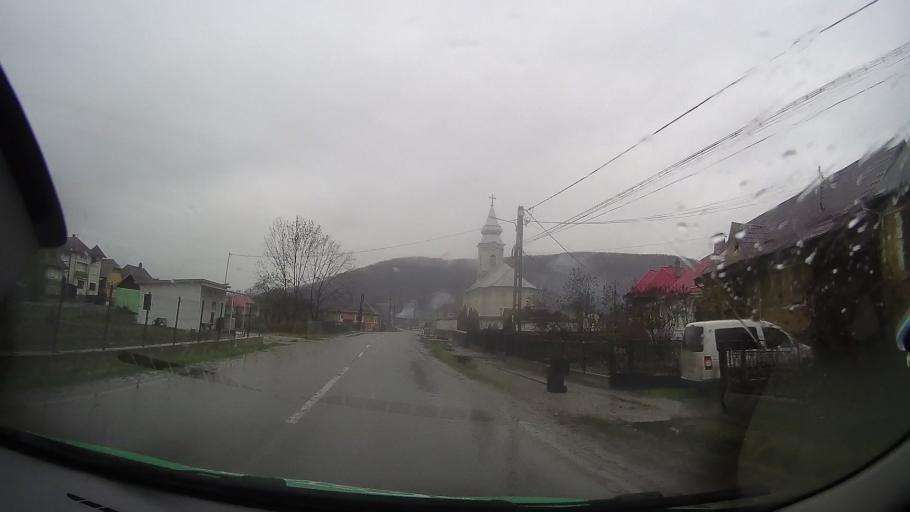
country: RO
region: Bistrita-Nasaud
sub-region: Comuna Sieut
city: Sieut
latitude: 46.9758
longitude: 24.6493
